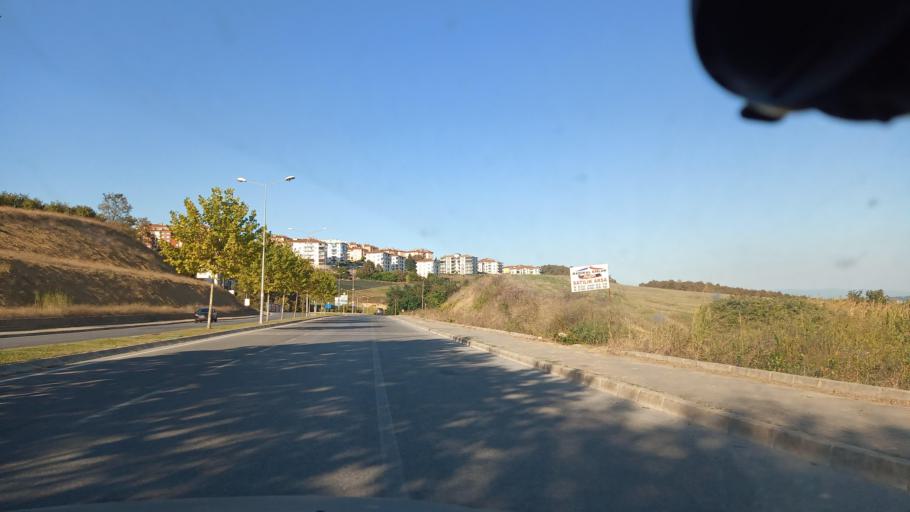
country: TR
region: Sakarya
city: Kazimpasa
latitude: 40.8524
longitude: 30.2872
